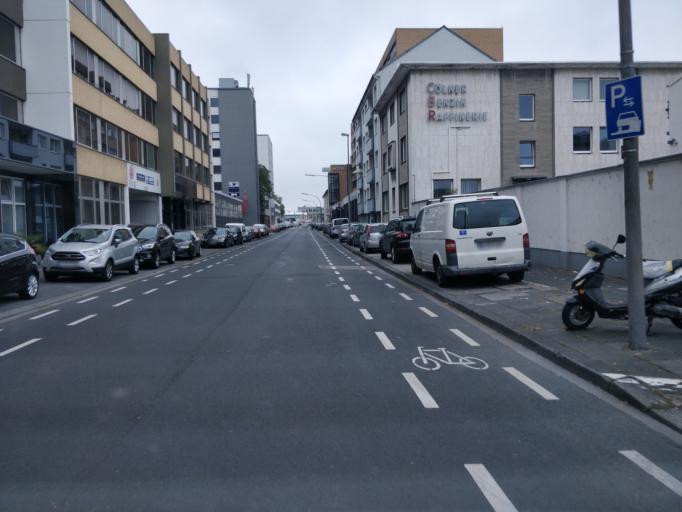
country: DE
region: North Rhine-Westphalia
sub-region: Regierungsbezirk Koln
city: Mengenich
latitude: 50.9444
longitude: 6.8897
